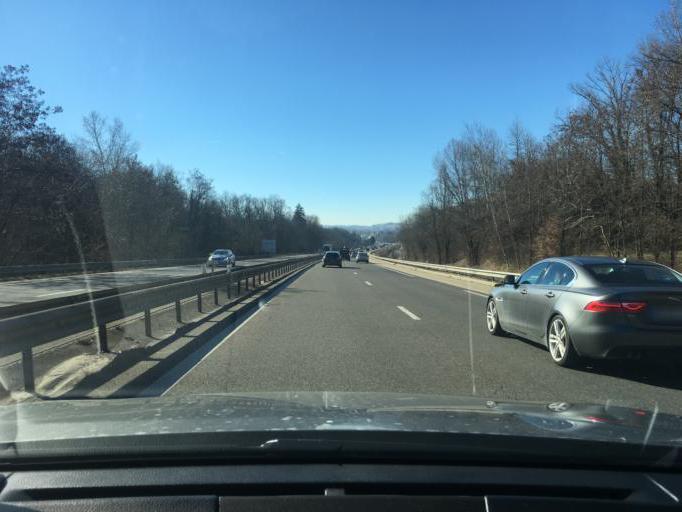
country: FR
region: Rhone-Alpes
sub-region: Departement de la Haute-Savoie
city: Metz-Tessy
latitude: 45.9295
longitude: 6.1117
